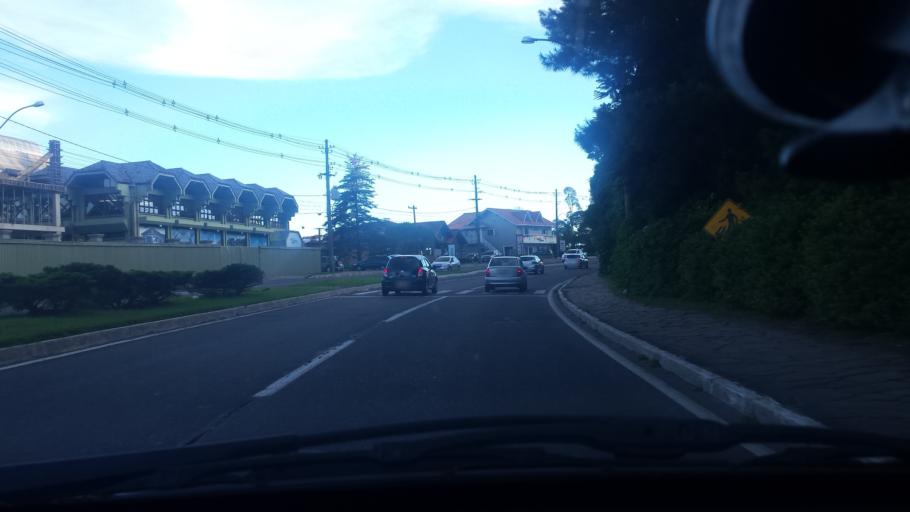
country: BR
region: Rio Grande do Sul
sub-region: Canela
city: Canela
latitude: -29.3758
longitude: -50.8645
